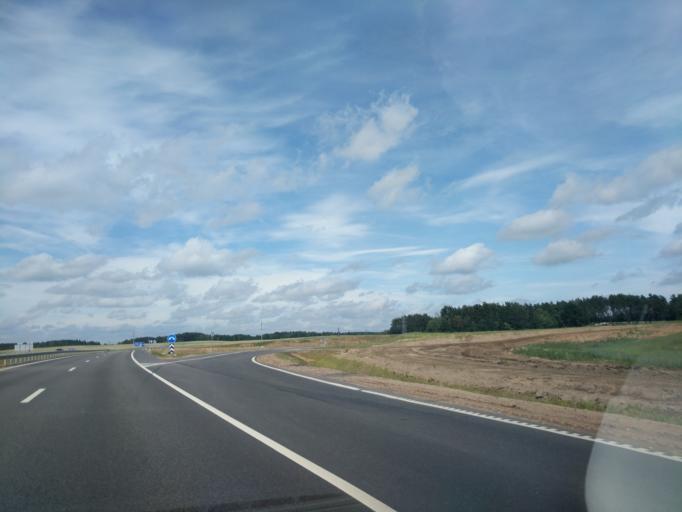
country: BY
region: Minsk
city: Bal'shavik
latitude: 54.0494
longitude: 27.5655
